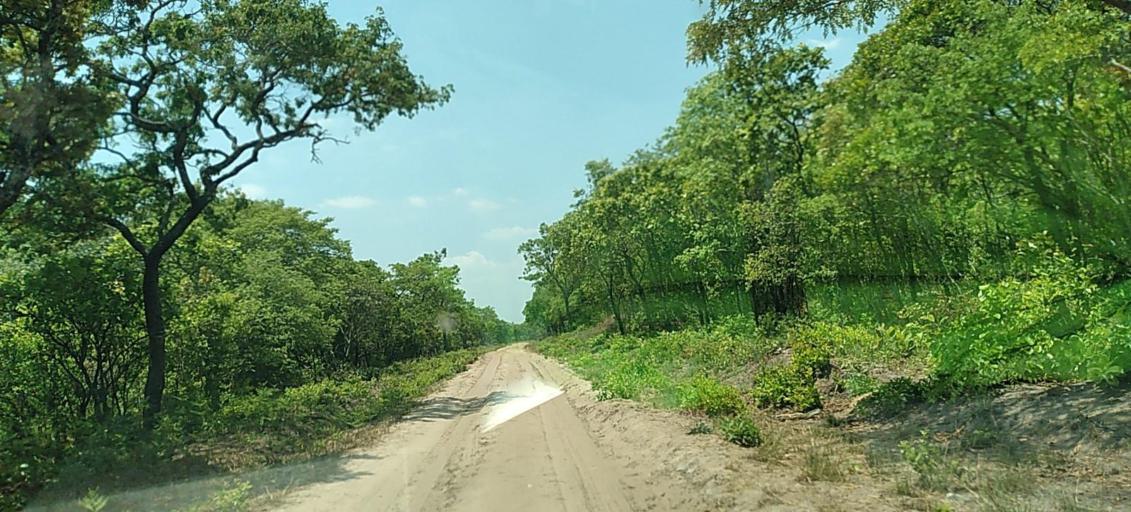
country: CD
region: Katanga
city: Kolwezi
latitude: -11.3406
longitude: 25.2195
